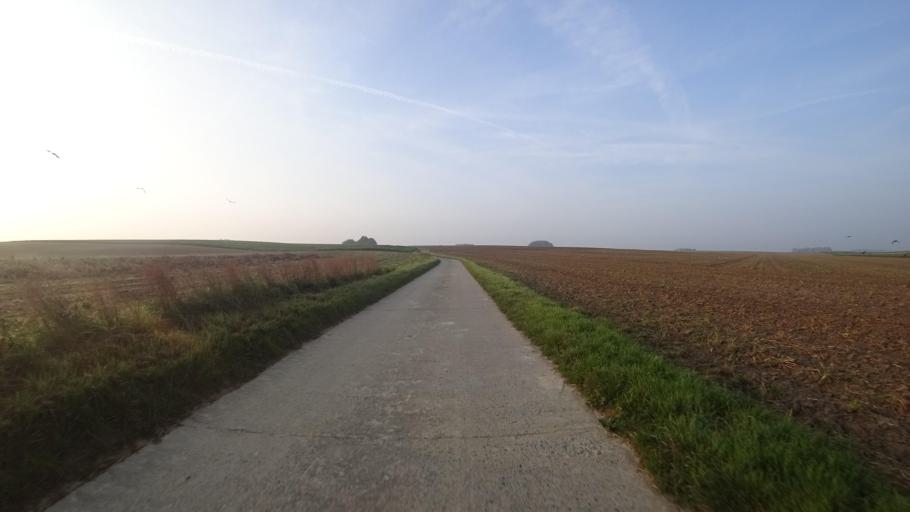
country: BE
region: Wallonia
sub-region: Province du Brabant Wallon
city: Walhain-Saint-Paul
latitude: 50.6369
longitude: 4.6944
